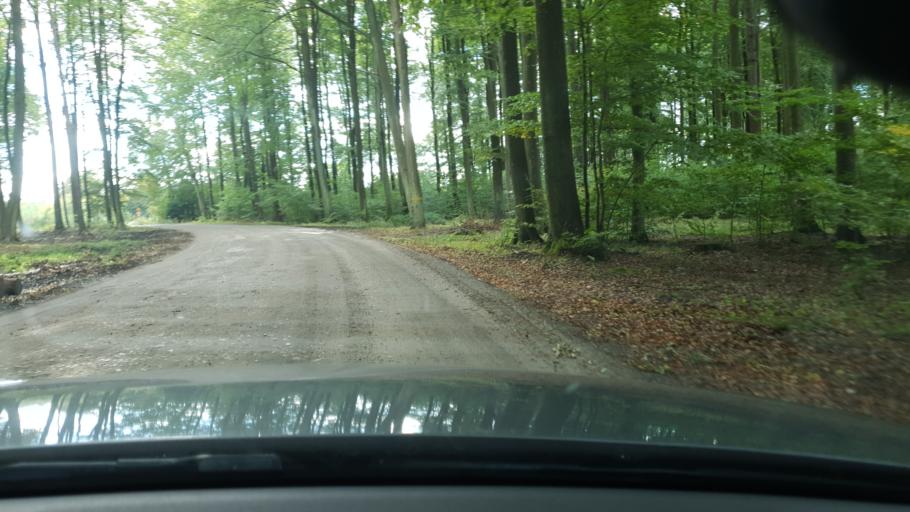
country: PL
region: Pomeranian Voivodeship
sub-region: Powiat wejherowski
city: Reda
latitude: 54.5829
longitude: 18.3137
